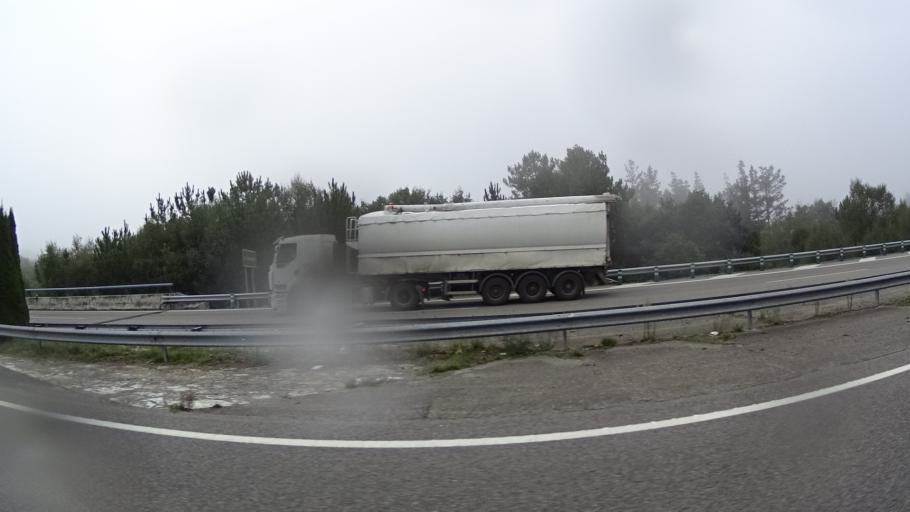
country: ES
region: Galicia
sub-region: Provincia de Lugo
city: Guitiriz
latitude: 43.1913
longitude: -7.8864
